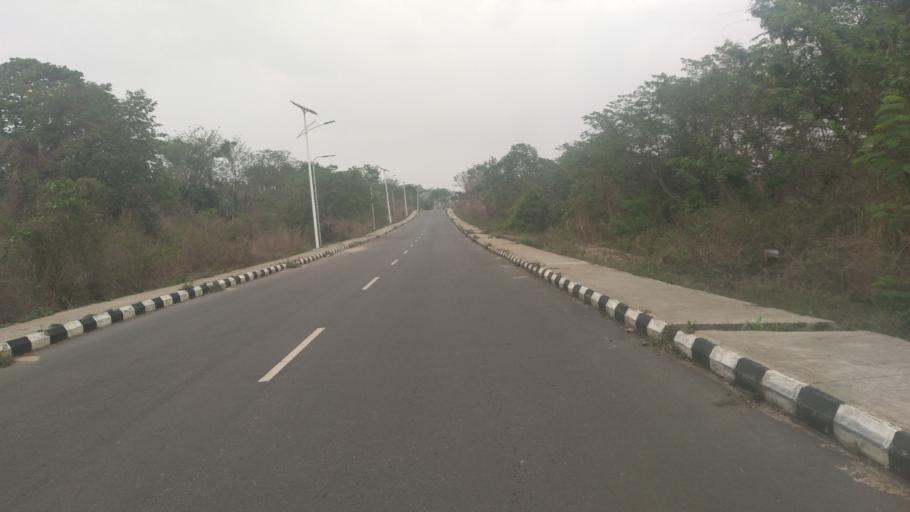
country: NG
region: Ondo
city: Ilare
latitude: 7.2954
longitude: 5.1376
